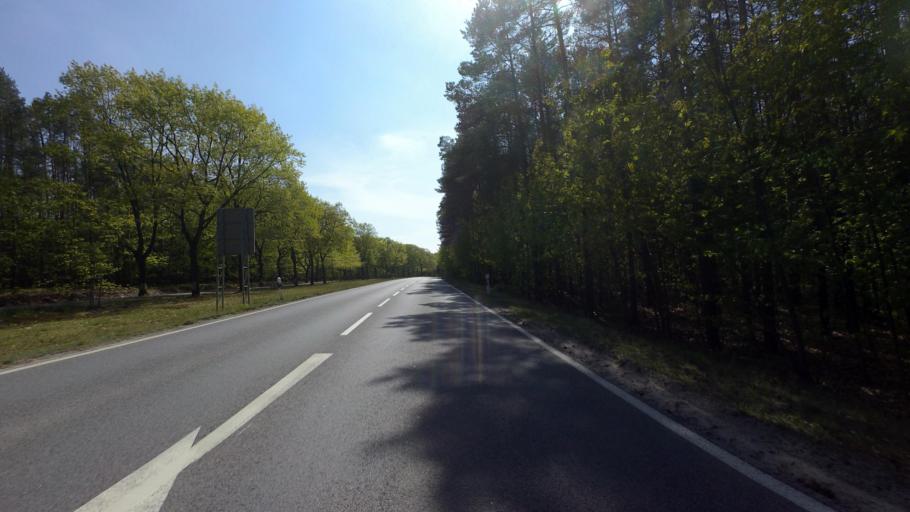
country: DE
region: Saxony
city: Ossling
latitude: 51.3736
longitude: 14.1996
